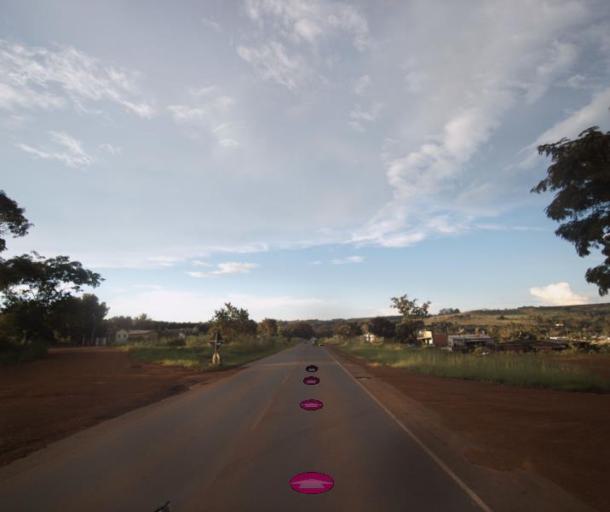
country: BR
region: Goias
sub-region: Anapolis
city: Anapolis
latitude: -16.2538
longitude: -48.9359
